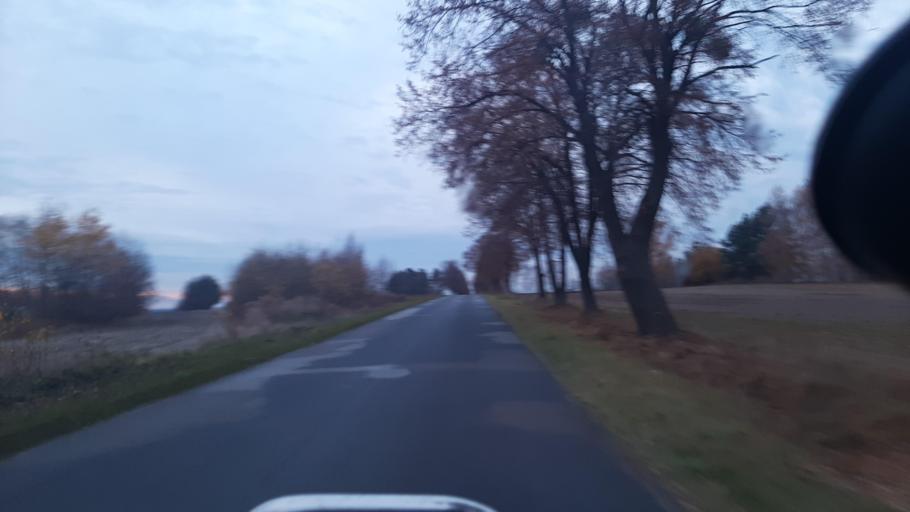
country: PL
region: Lublin Voivodeship
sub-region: Powiat lubelski
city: Garbow
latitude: 51.3800
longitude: 22.3783
